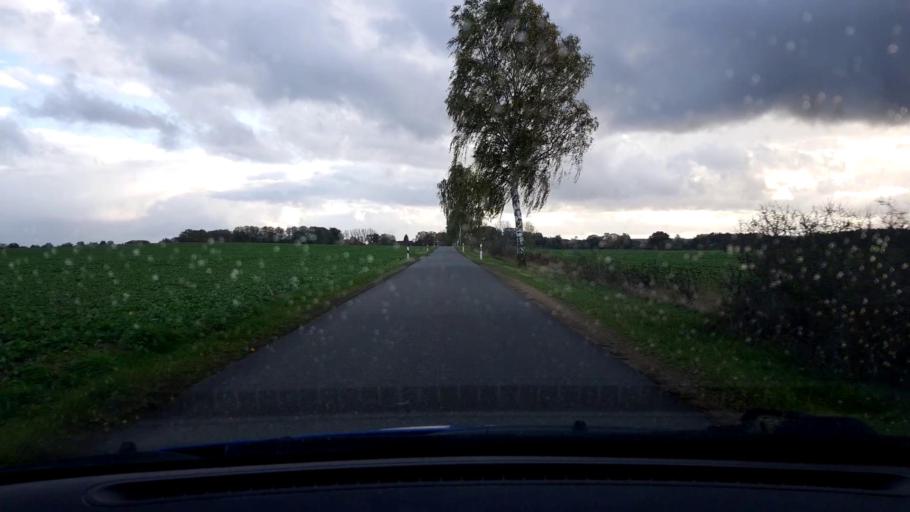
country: DE
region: Lower Saxony
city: Reinstorf
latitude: 53.2589
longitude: 10.5645
